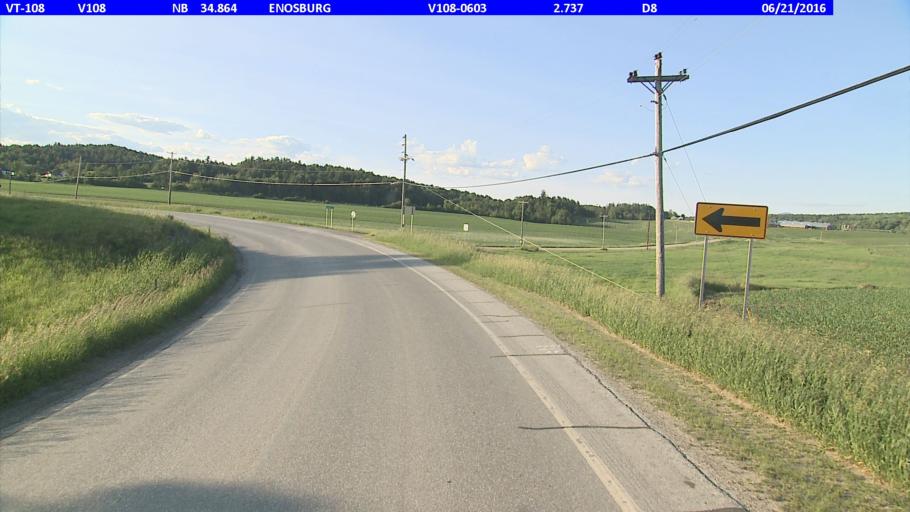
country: US
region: Vermont
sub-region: Franklin County
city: Enosburg Falls
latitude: 44.8768
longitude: -72.7951
